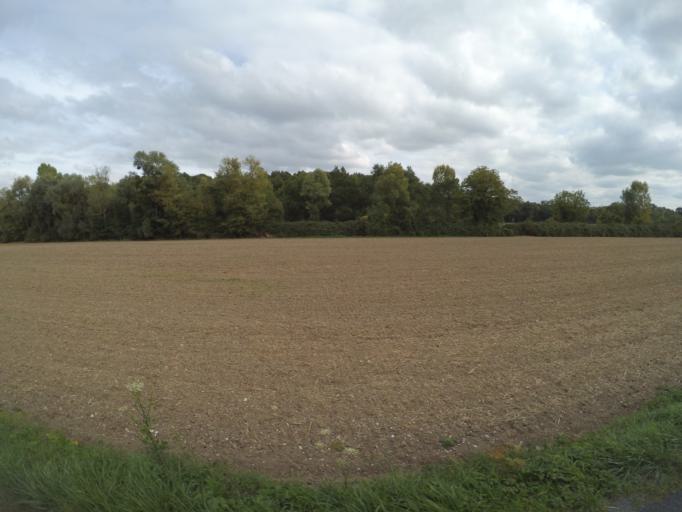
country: FR
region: Centre
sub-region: Departement d'Indre-et-Loire
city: Reugny
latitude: 47.4633
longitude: 0.8791
